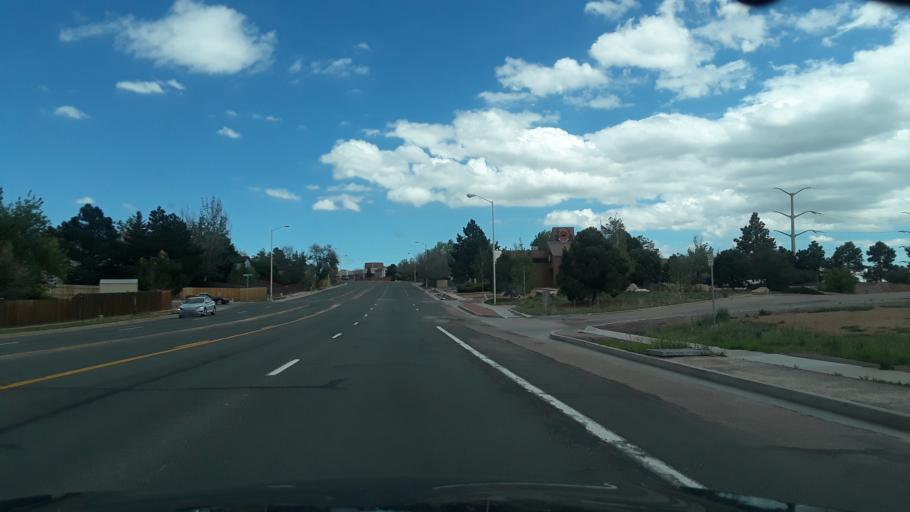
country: US
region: Colorado
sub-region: El Paso County
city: Air Force Academy
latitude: 38.9436
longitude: -104.7821
